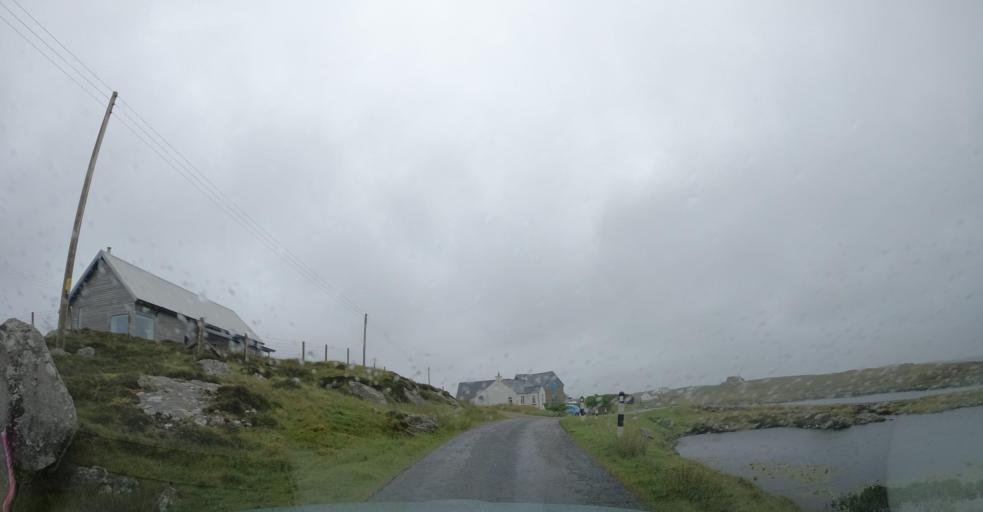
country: GB
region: Scotland
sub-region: Eilean Siar
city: Benbecula
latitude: 57.4865
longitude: -7.2190
